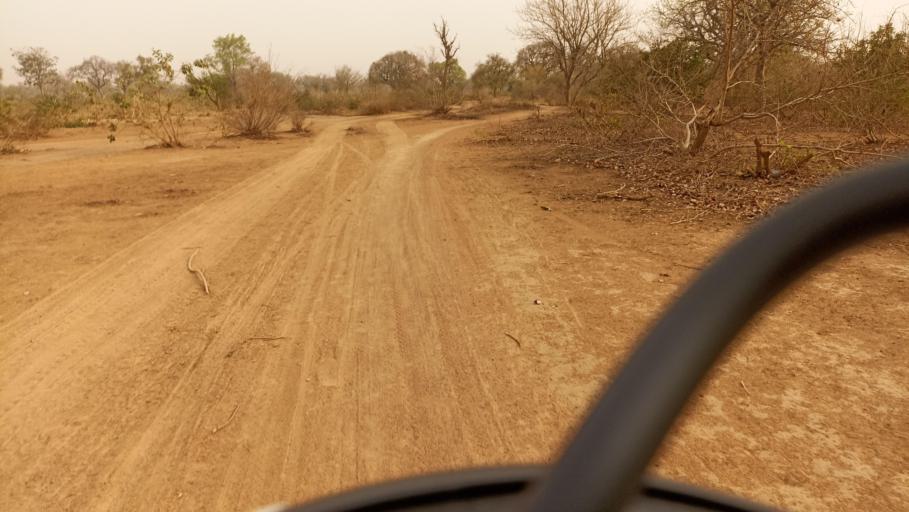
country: BF
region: Nord
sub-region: Province du Zondoma
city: Gourcy
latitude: 13.1610
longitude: -2.5933
